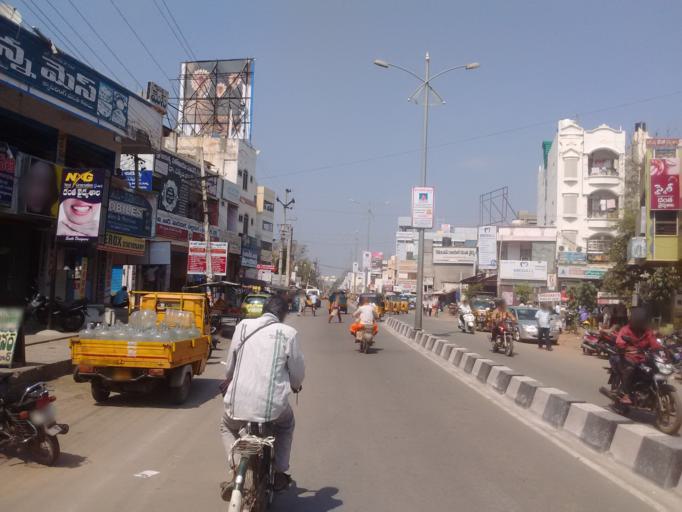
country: IN
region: Telangana
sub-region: Mahbubnagar
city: Alampur
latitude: 15.8348
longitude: 78.0416
